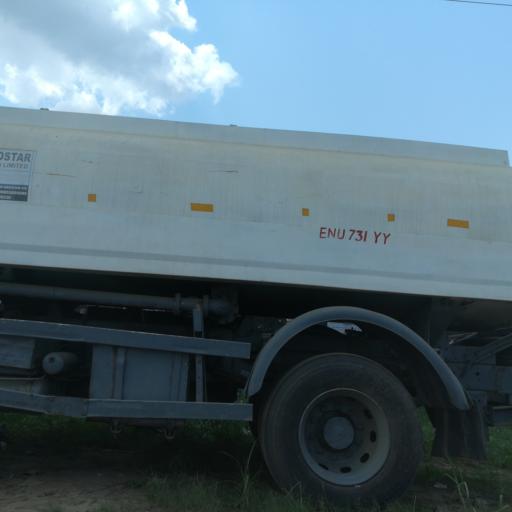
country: NG
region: Rivers
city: Okrika
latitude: 4.8952
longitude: 7.1215
